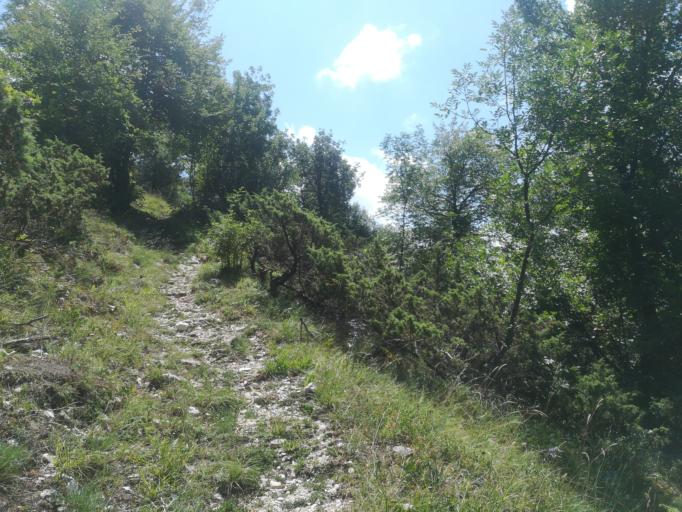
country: IT
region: Umbria
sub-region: Provincia di Perugia
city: Scheggino
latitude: 42.6732
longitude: 12.8552
